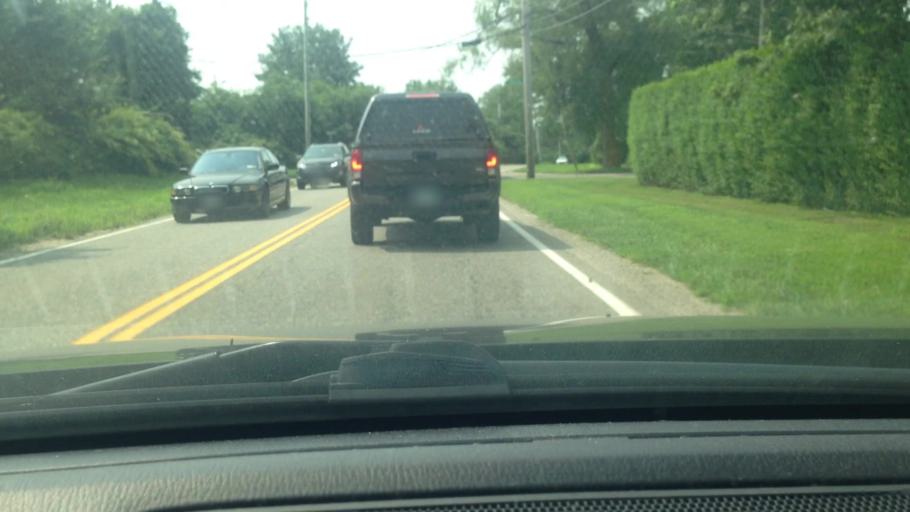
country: US
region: New York
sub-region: Suffolk County
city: Water Mill
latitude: 40.9391
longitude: -72.3372
